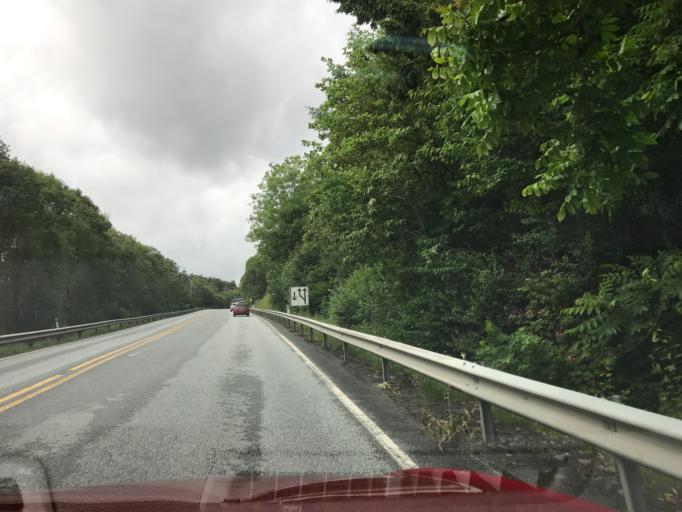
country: NO
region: Rogaland
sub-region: Tysvaer
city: Aksdal
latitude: 59.4215
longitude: 5.4191
